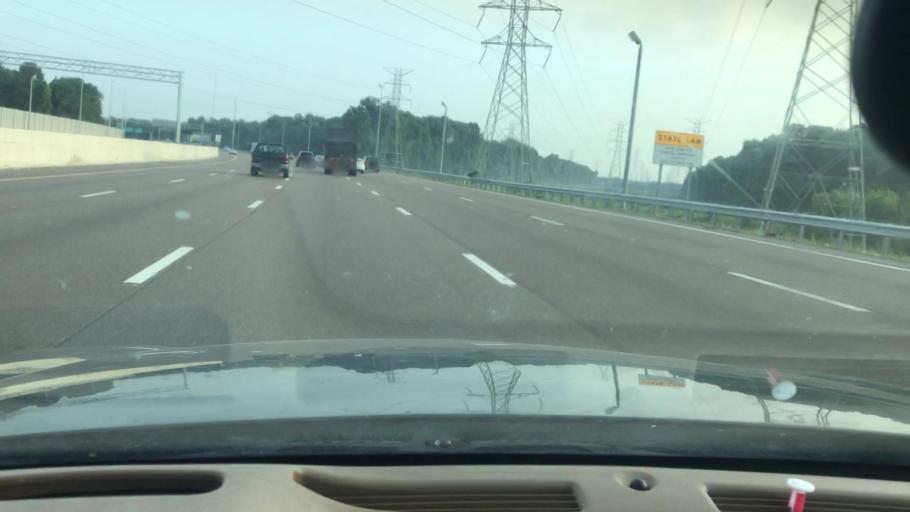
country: US
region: Tennessee
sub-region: Shelby County
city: Bartlett
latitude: 35.1369
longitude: -89.8681
